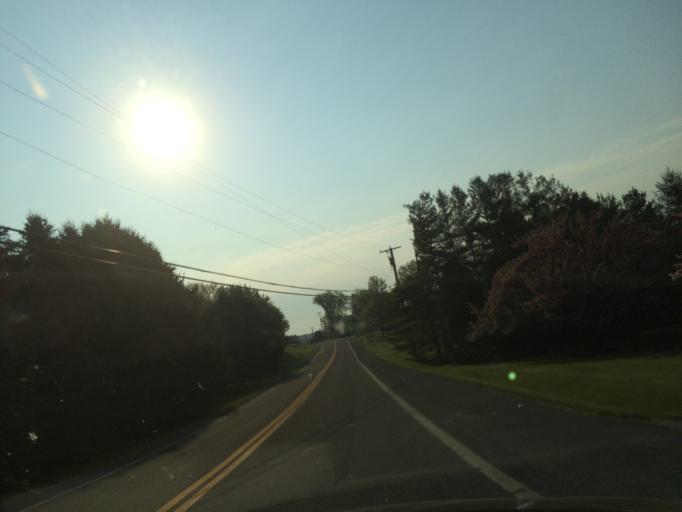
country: US
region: Maryland
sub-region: Carroll County
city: Sykesville
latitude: 39.3947
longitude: -77.0248
